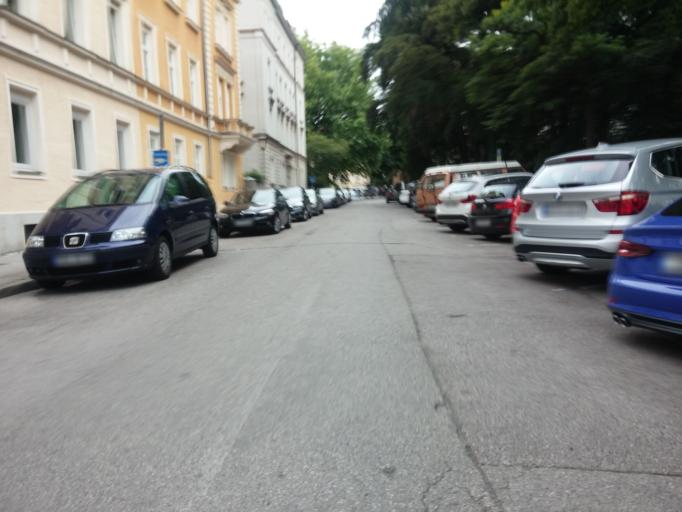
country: DE
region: Bavaria
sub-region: Upper Bavaria
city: Munich
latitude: 48.1355
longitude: 11.5962
